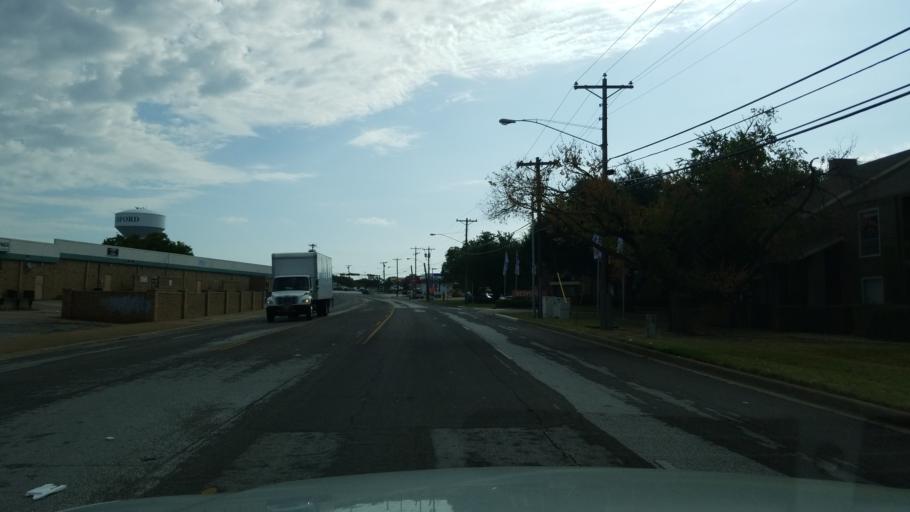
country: US
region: Texas
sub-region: Tarrant County
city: Hurst
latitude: 32.8340
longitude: -97.1638
